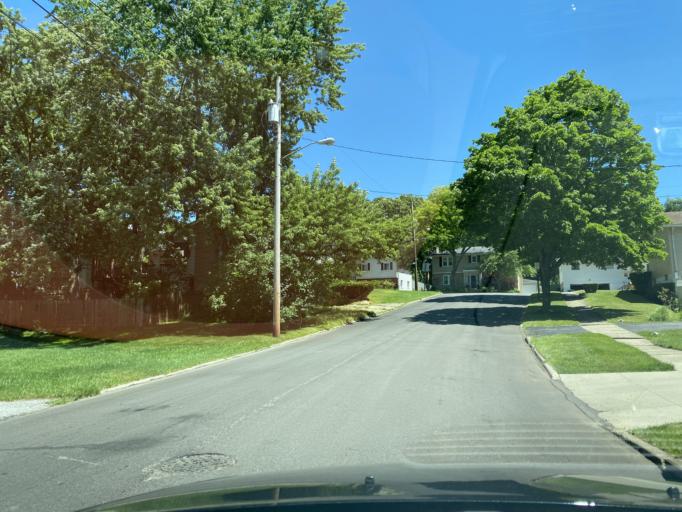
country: US
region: Ohio
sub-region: Summit County
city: Fairlawn
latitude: 41.1275
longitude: -81.5662
